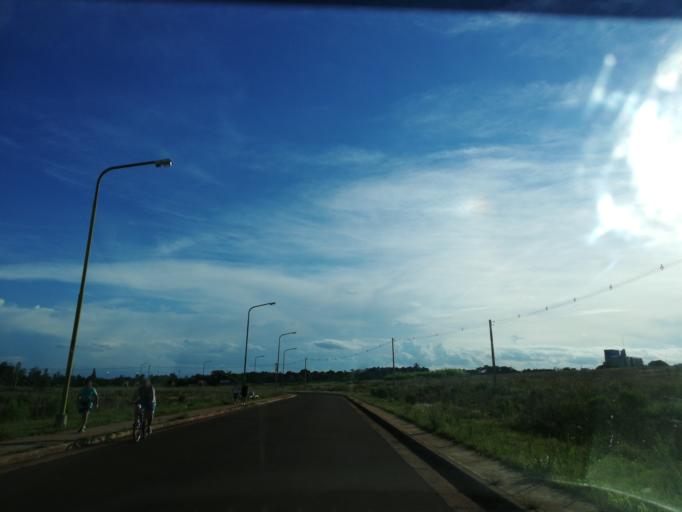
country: AR
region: Misiones
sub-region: Departamento de Capital
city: Posadas
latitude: -27.3931
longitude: -55.9554
